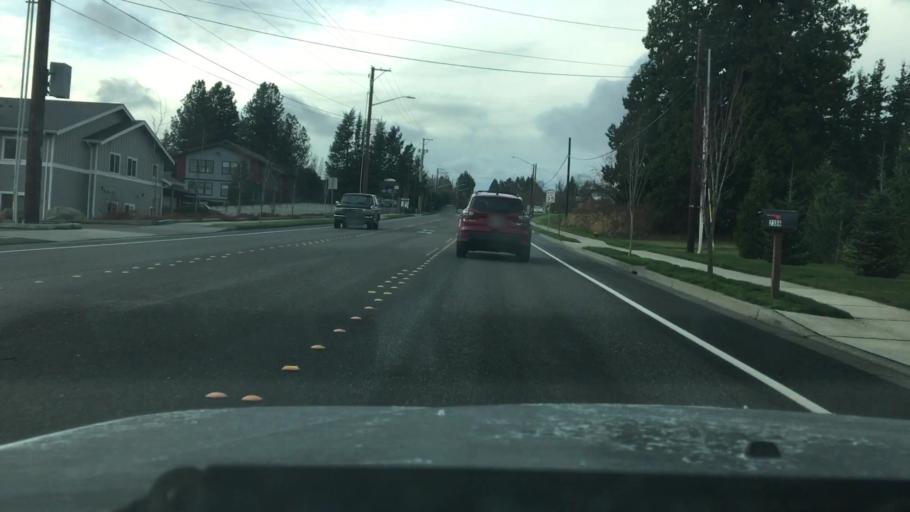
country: US
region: Washington
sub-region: Whatcom County
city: Ferndale
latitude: 48.8484
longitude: -122.6112
